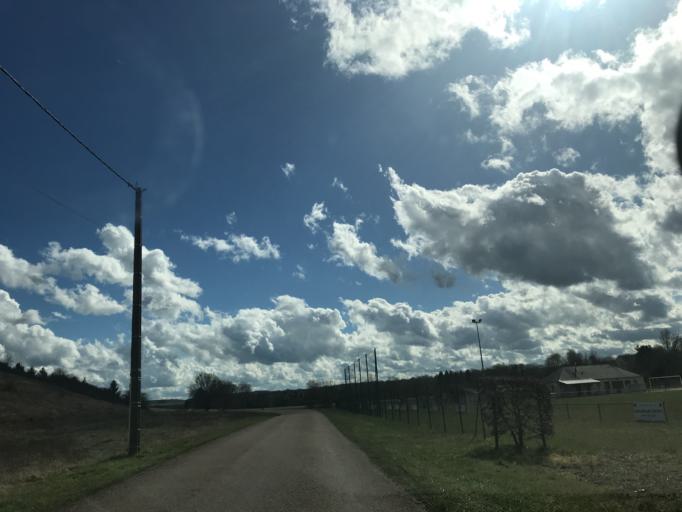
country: FR
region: Bourgogne
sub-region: Departement de l'Yonne
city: Fontenailles
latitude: 47.5183
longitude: 3.4916
